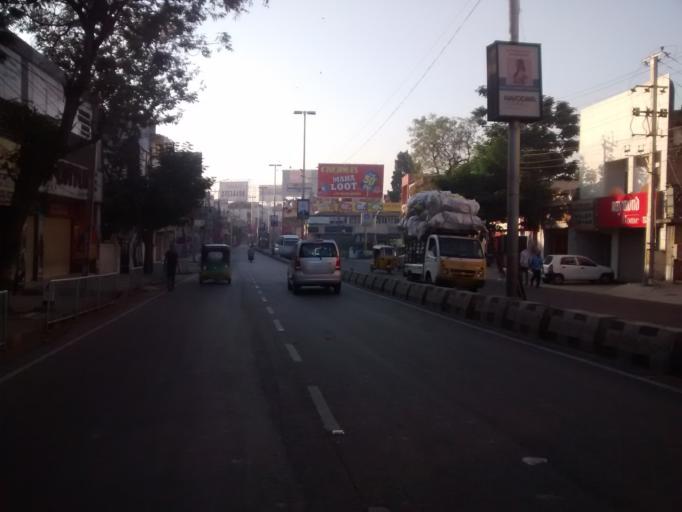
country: IN
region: Telangana
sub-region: Hyderabad
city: Malkajgiri
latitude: 17.4404
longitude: 78.4880
